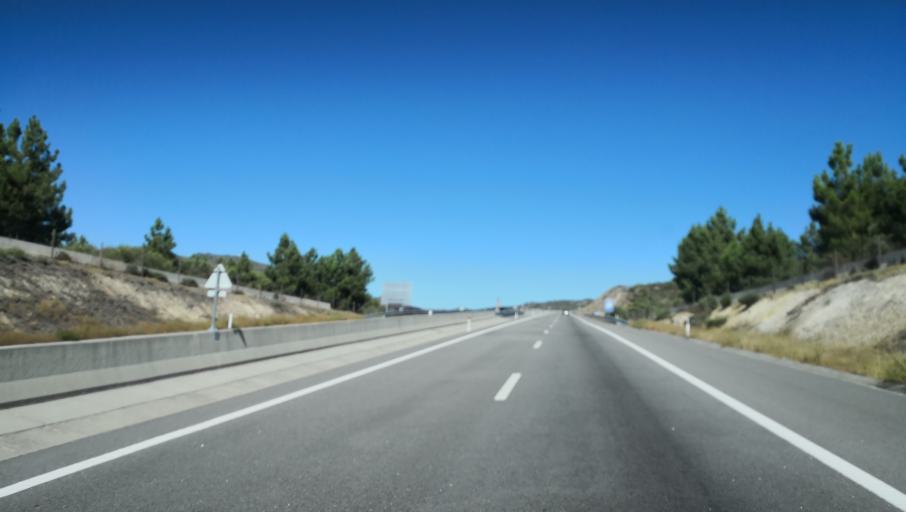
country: PT
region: Vila Real
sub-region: Sabrosa
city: Sabrosa
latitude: 41.3658
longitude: -7.5577
